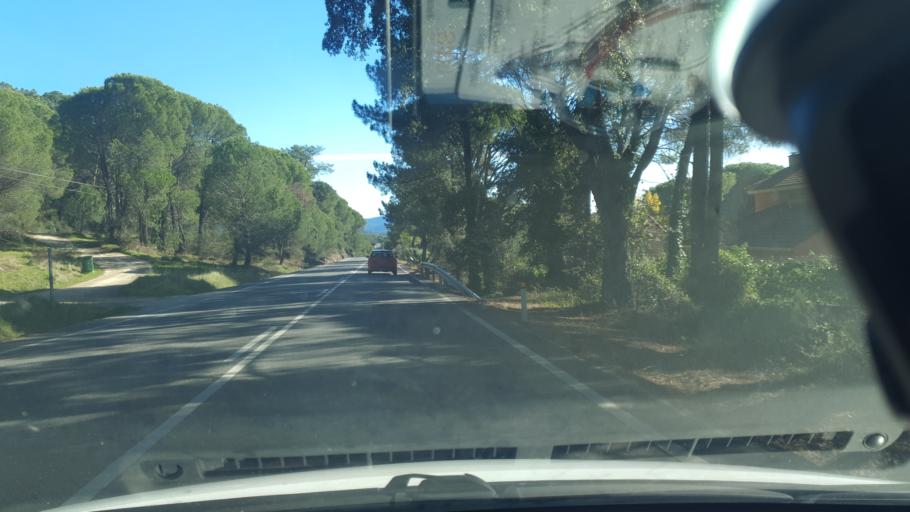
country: ES
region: Castille and Leon
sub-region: Provincia de Avila
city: Piedralaves
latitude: 40.3160
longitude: -4.6785
